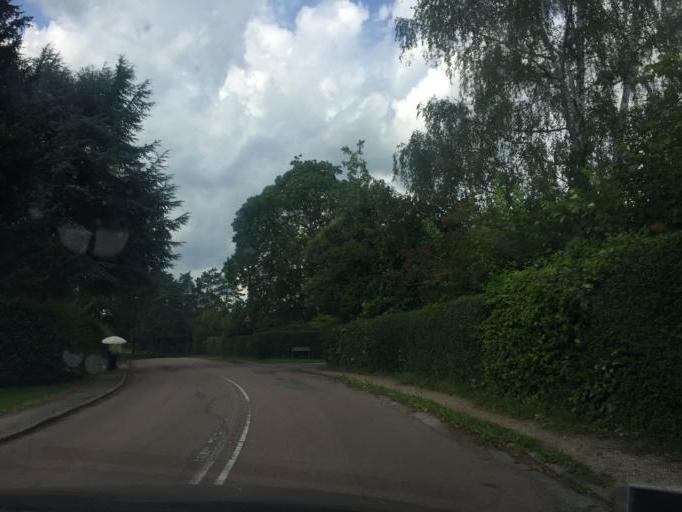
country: DK
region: Capital Region
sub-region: Rudersdal Kommune
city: Holte
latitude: 55.7926
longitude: 12.4516
